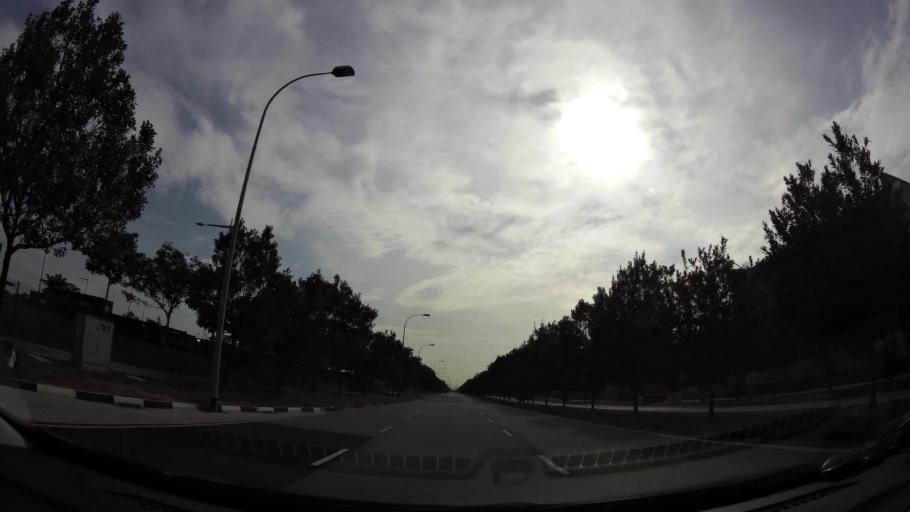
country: SG
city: Singapore
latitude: 1.2750
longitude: 103.6244
